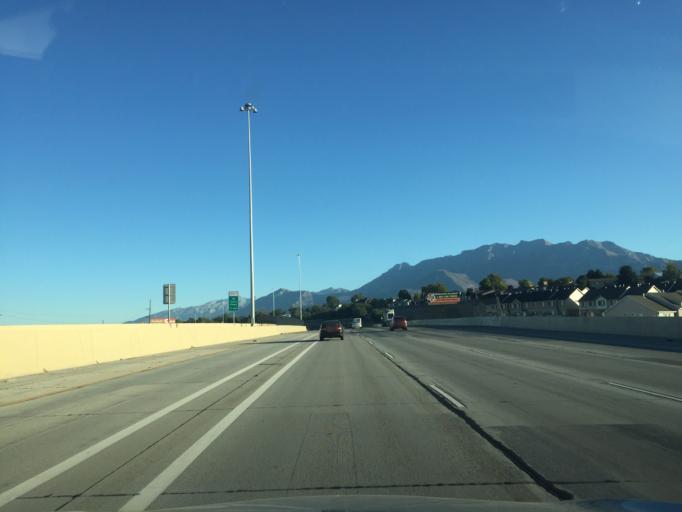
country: US
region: Utah
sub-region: Utah County
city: Provo
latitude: 40.2474
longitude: -111.6952
